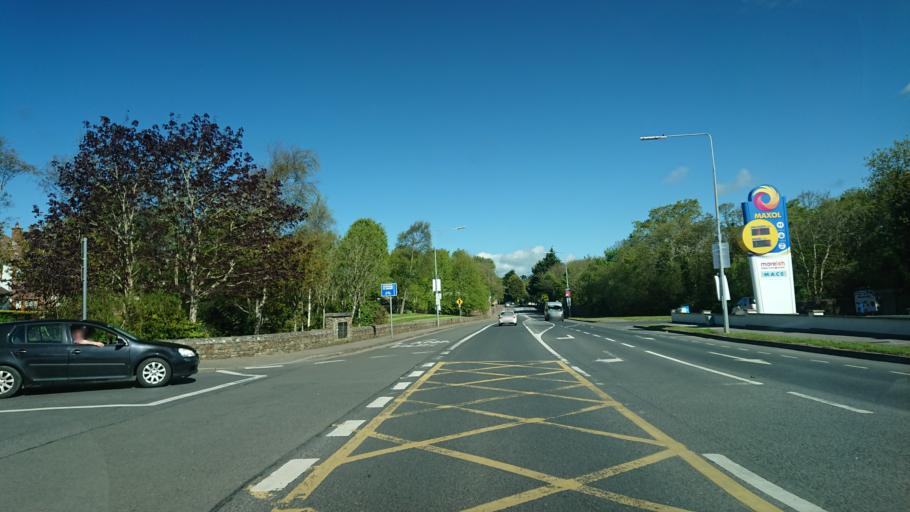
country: IE
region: Munster
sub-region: Waterford
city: Waterford
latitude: 52.2424
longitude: -7.0698
